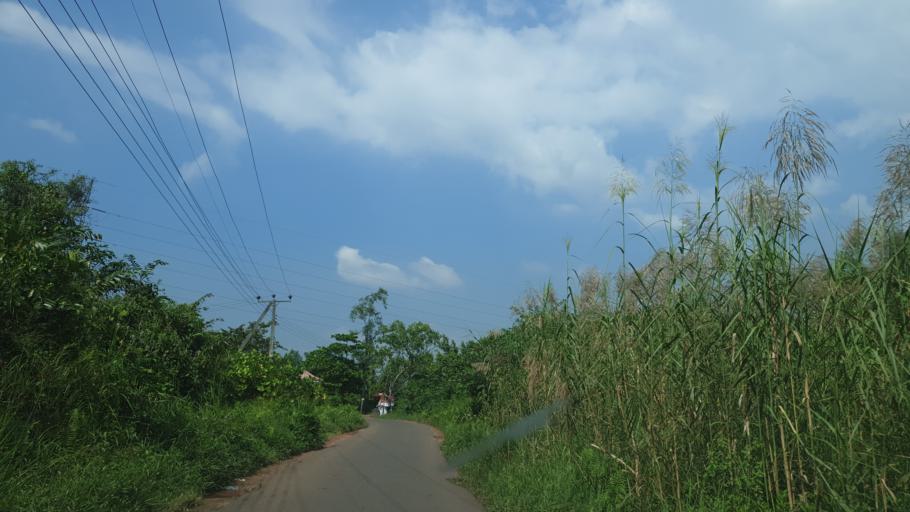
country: LK
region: Western
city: Panadura
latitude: 6.7401
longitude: 79.9514
